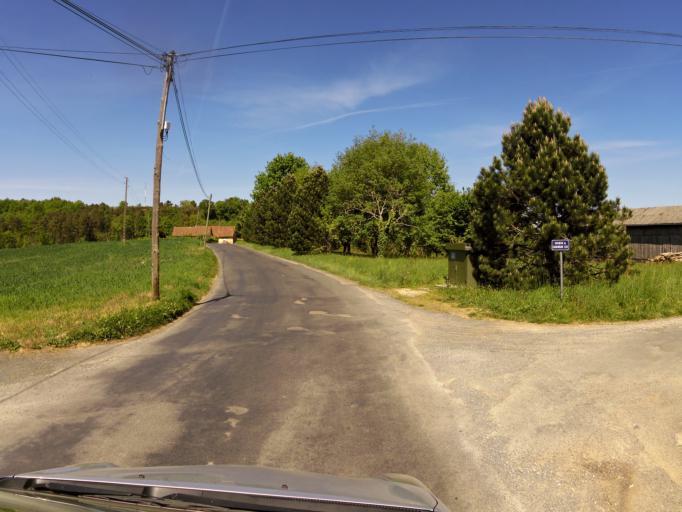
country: FR
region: Aquitaine
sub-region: Departement de la Dordogne
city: Sarlat-la-Caneda
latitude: 44.9184
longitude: 1.1965
